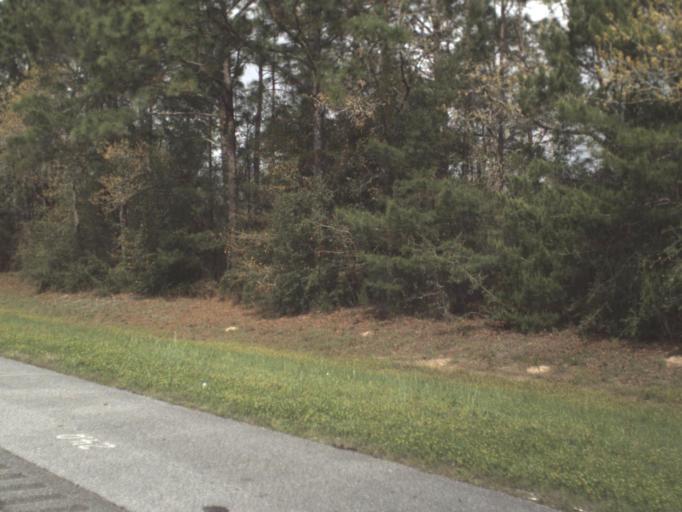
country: US
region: Florida
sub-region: Okaloosa County
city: Crestview
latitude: 30.7274
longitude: -86.4006
